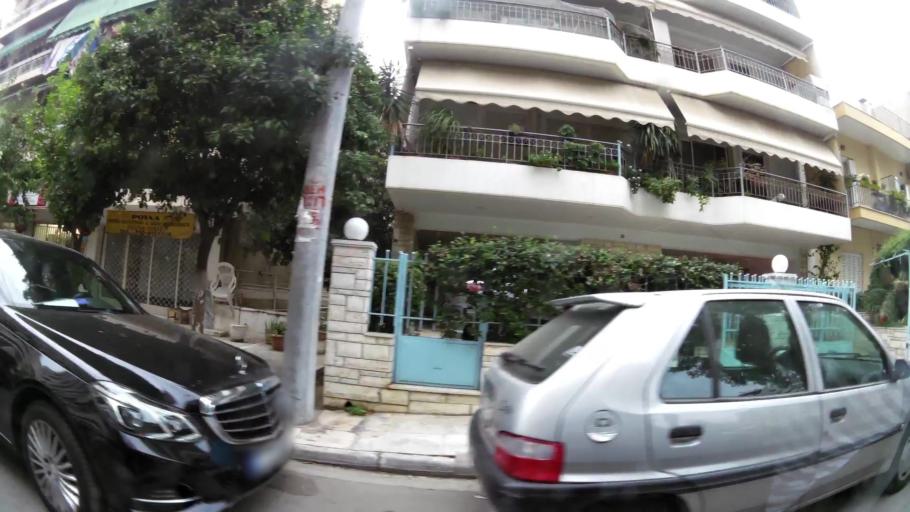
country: GR
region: Attica
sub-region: Nomos Piraios
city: Agios Ioannis Rentis
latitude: 37.9612
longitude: 23.6712
